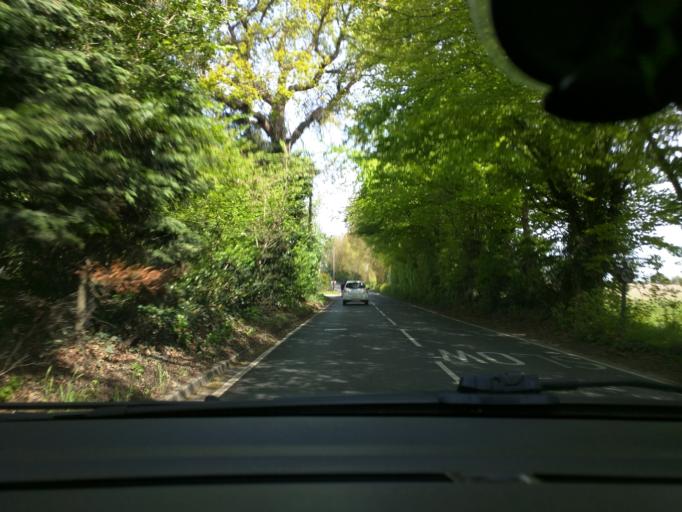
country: GB
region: England
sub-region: Suffolk
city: Leiston
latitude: 52.2384
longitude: 1.5669
